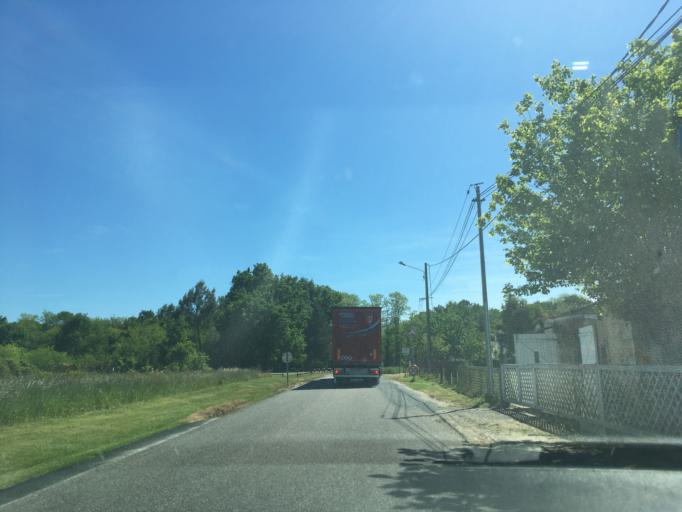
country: FR
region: Aquitaine
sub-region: Departement de la Gironde
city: Lesparre-Medoc
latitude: 45.2707
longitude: -0.8890
